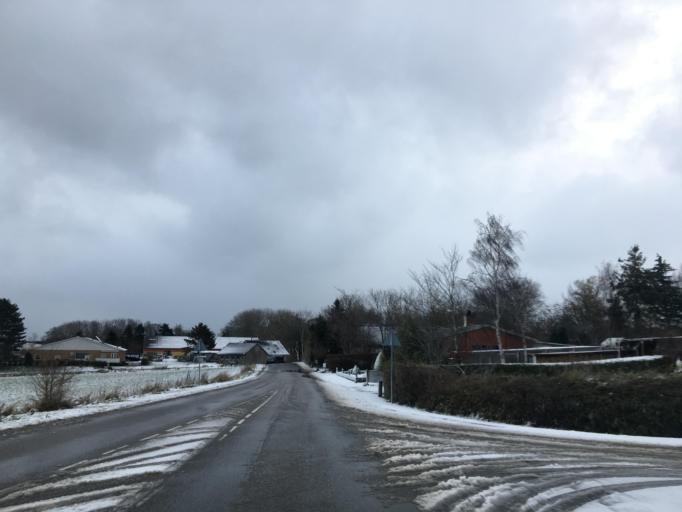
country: DK
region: Zealand
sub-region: Odsherred Kommune
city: Asnaes
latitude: 55.8310
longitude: 11.5637
